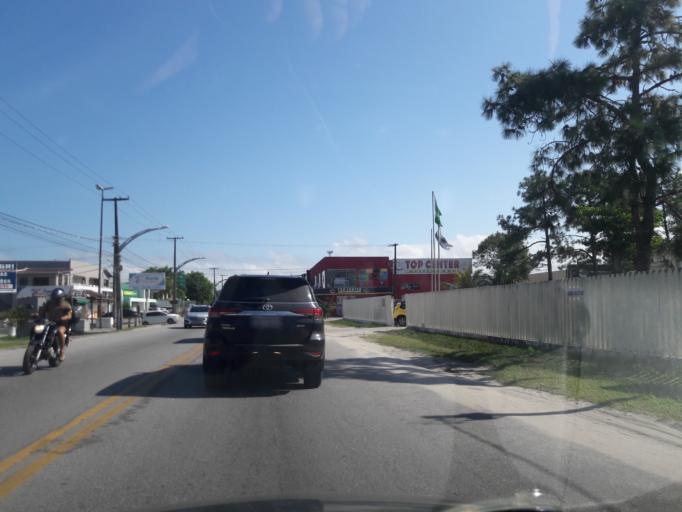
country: BR
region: Parana
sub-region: Pontal Do Parana
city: Pontal do Parana
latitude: -25.6928
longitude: -48.4736
